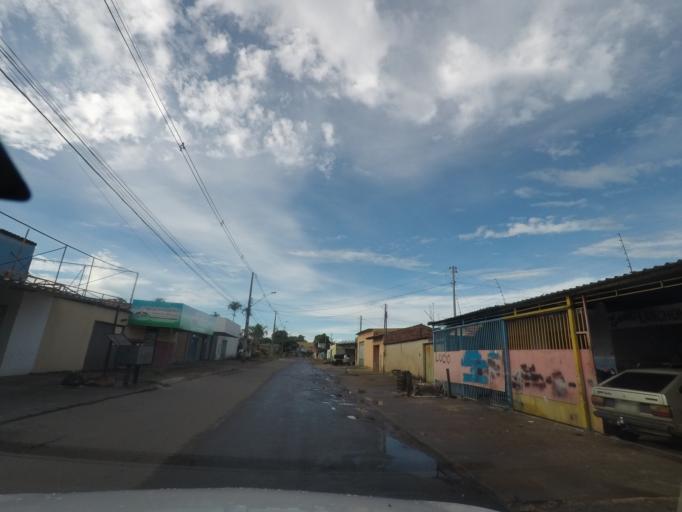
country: BR
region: Goias
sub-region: Aparecida De Goiania
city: Aparecida de Goiania
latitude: -16.7663
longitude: -49.3520
